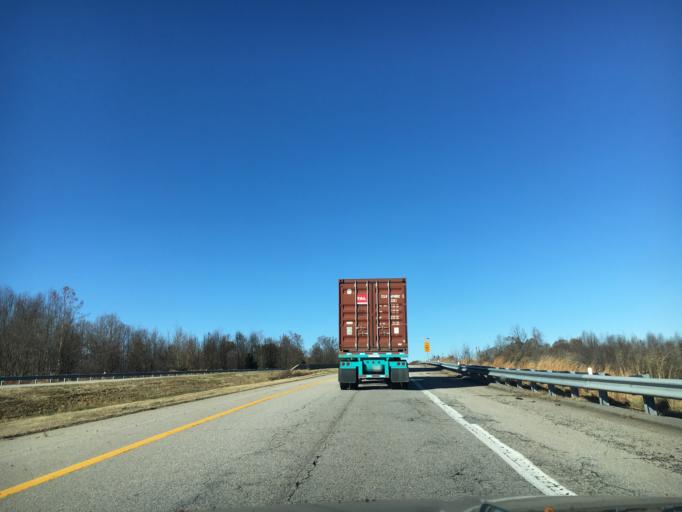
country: US
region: Virginia
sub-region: Pittsylvania County
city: Mount Hermon
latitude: 36.6026
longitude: -79.5362
